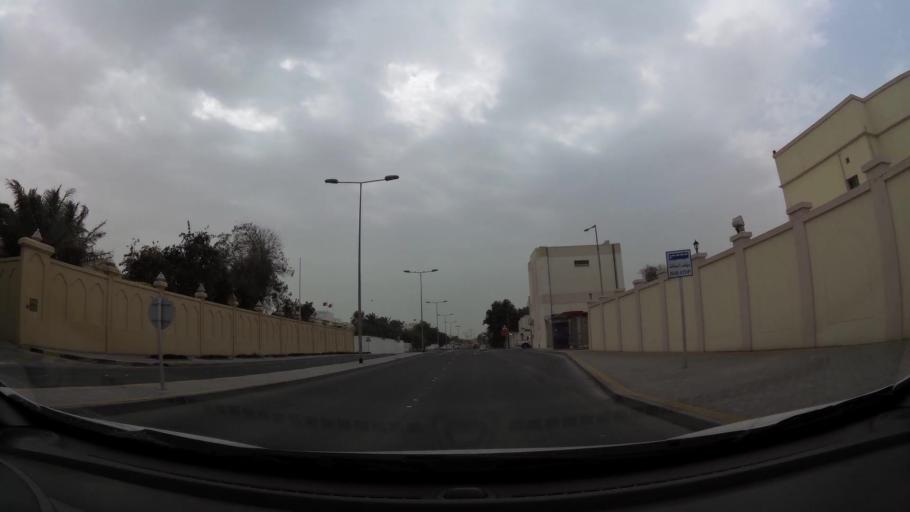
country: BH
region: Northern
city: Ar Rifa'
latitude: 26.1277
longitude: 50.5493
